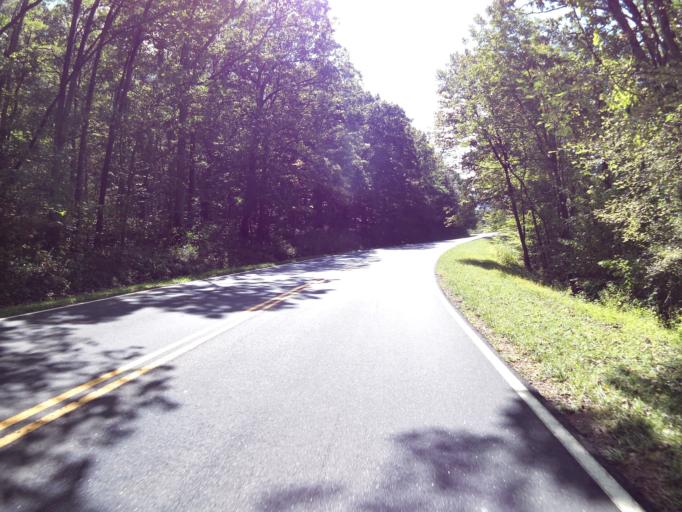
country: US
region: Virginia
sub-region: Rappahannock County
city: Washington
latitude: 38.7473
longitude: -78.3060
